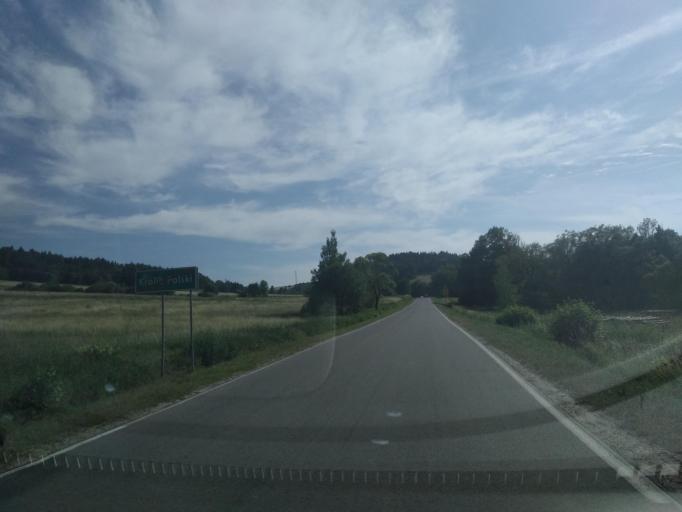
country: PL
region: Subcarpathian Voivodeship
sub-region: Powiat krosnienski
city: Jasliska
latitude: 49.5014
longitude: 21.8129
